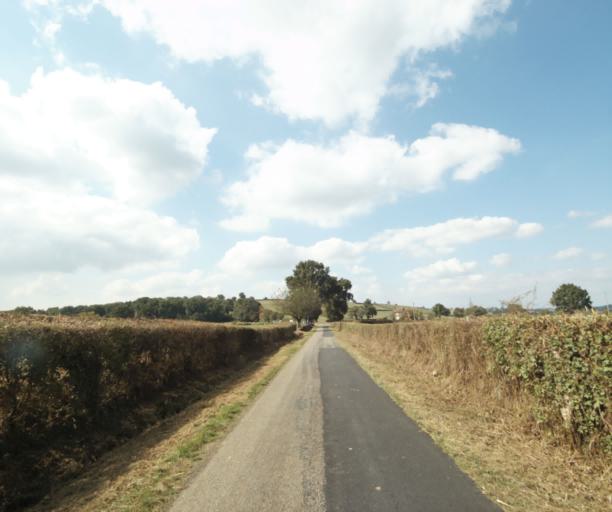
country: FR
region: Bourgogne
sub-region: Departement de Saone-et-Loire
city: Charolles
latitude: 46.3551
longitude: 4.2403
